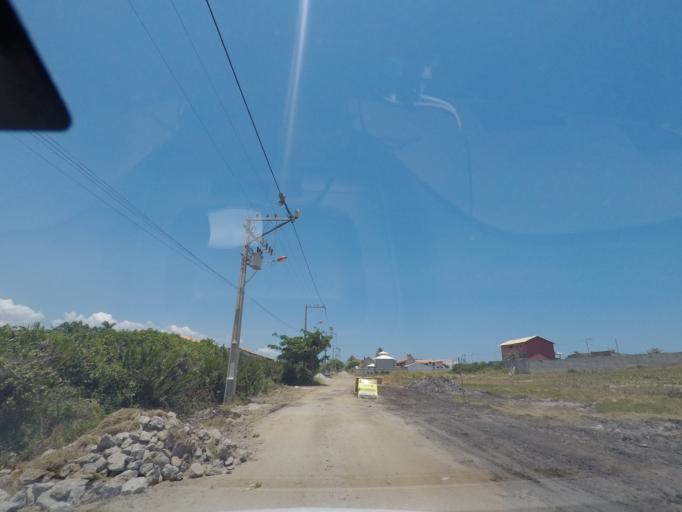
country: BR
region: Rio de Janeiro
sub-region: Niteroi
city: Niteroi
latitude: -22.9685
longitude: -42.9707
